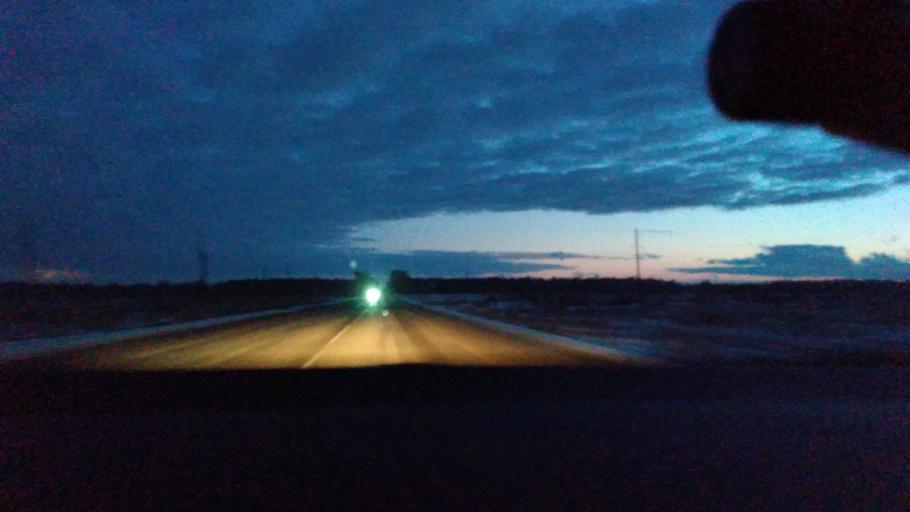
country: RU
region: Moskovskaya
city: Krasnaya Poyma
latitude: 55.1255
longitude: 39.1504
